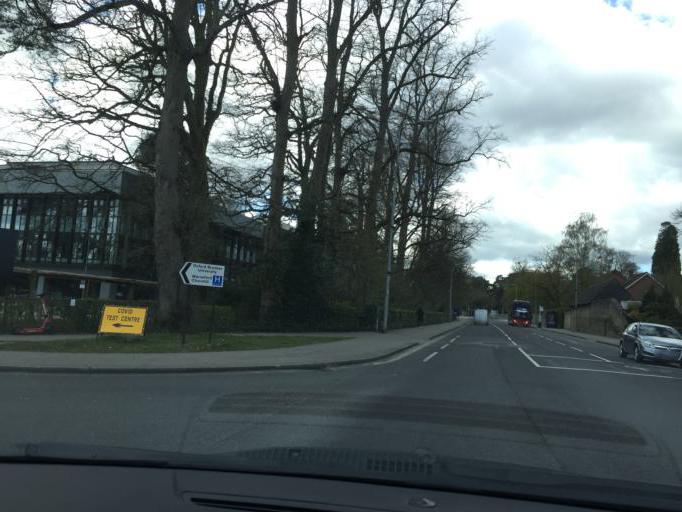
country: GB
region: England
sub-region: Oxfordshire
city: Cowley
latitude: 51.7564
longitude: -1.2233
